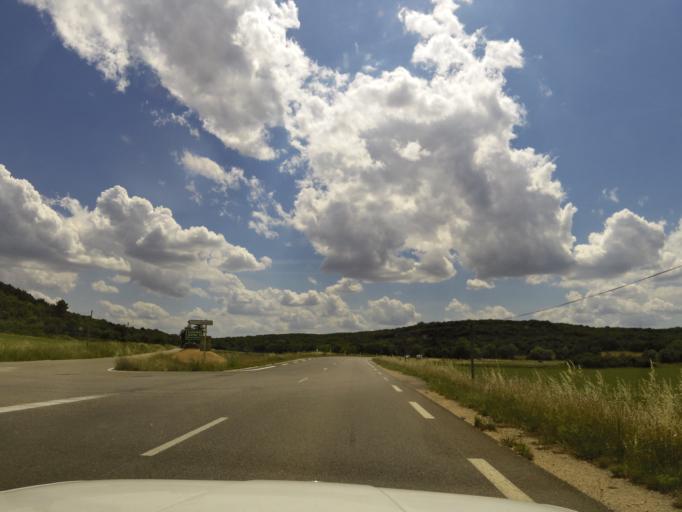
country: FR
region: Languedoc-Roussillon
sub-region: Departement du Gard
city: Montaren-et-Saint-Mediers
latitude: 44.1303
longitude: 4.3314
